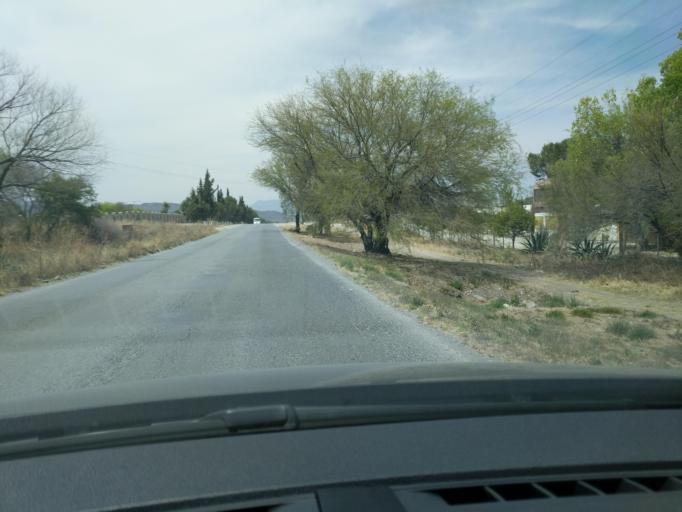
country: MX
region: Coahuila
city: Saltillo
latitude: 25.3542
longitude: -101.0274
